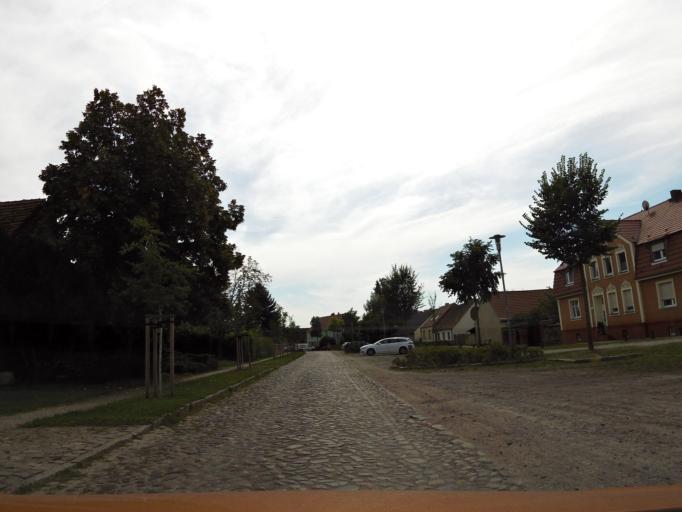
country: DE
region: Brandenburg
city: Michendorf
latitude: 52.2454
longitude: 13.0800
